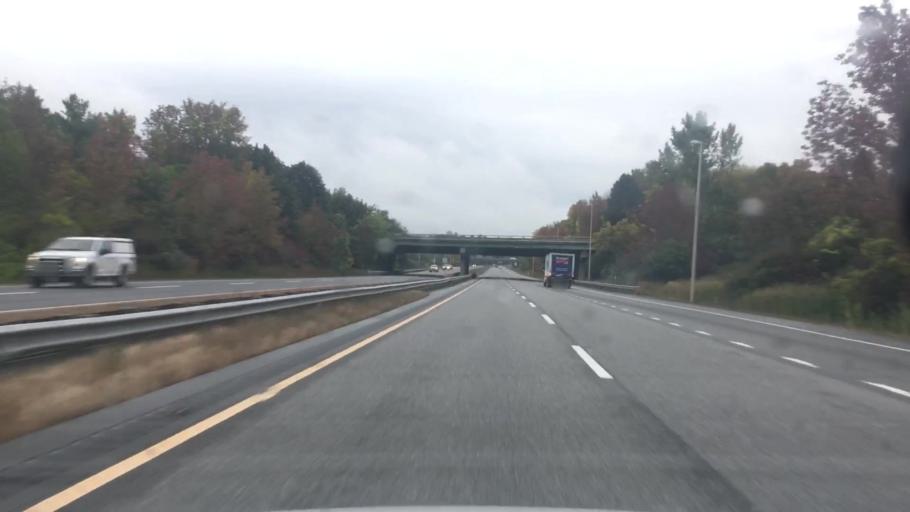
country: US
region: Maine
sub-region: Kennebec County
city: Augusta
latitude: 44.3151
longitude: -69.8109
